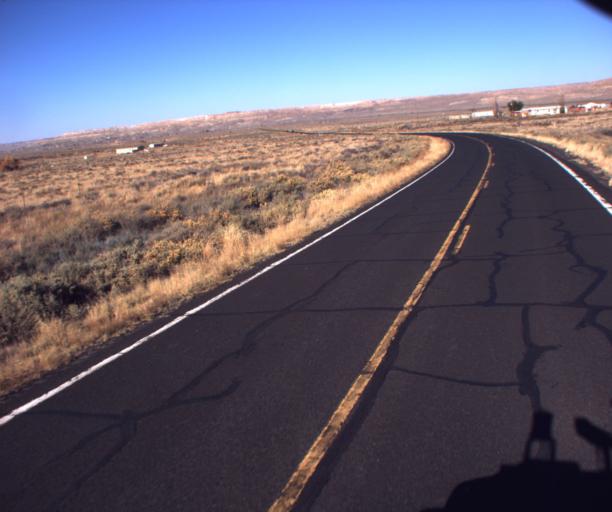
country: US
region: Arizona
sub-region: Navajo County
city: First Mesa
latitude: 35.8380
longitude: -110.3036
